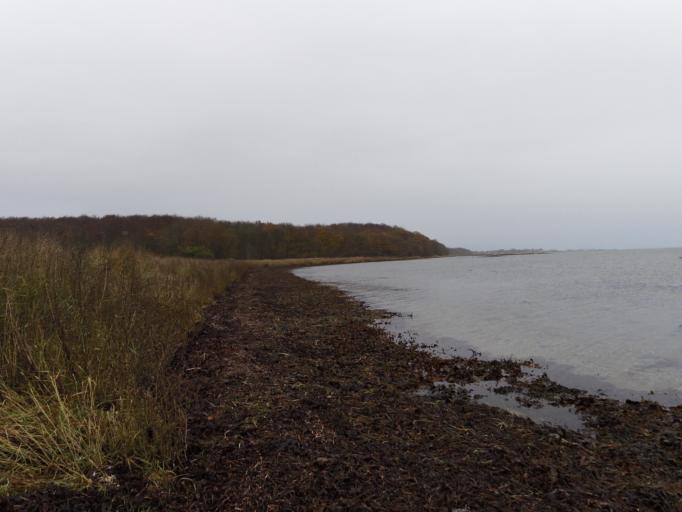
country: DK
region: Central Jutland
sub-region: Odder Kommune
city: Odder
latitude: 55.8985
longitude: 10.2238
